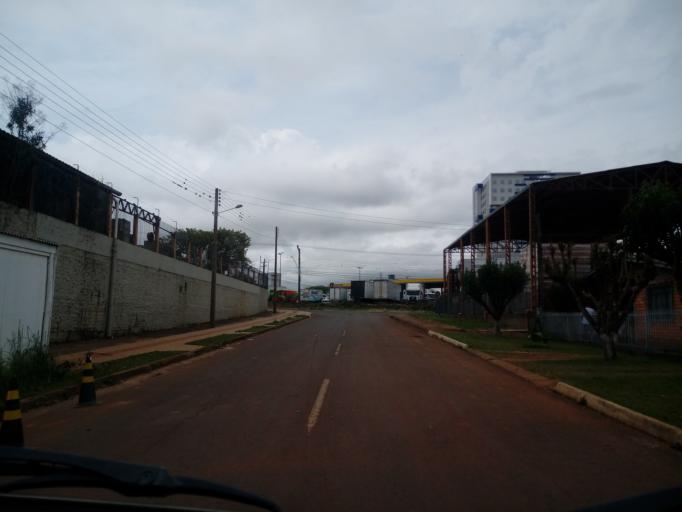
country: BR
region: Santa Catarina
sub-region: Chapeco
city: Chapeco
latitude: -27.0723
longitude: -52.6281
